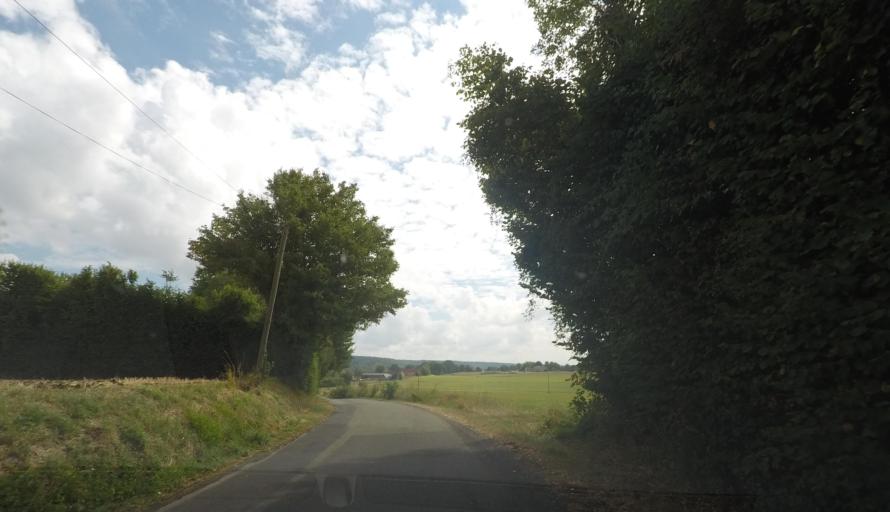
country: FR
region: Pays de la Loire
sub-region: Departement de la Sarthe
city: La Ferte-Bernard
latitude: 48.2657
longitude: 0.5968
